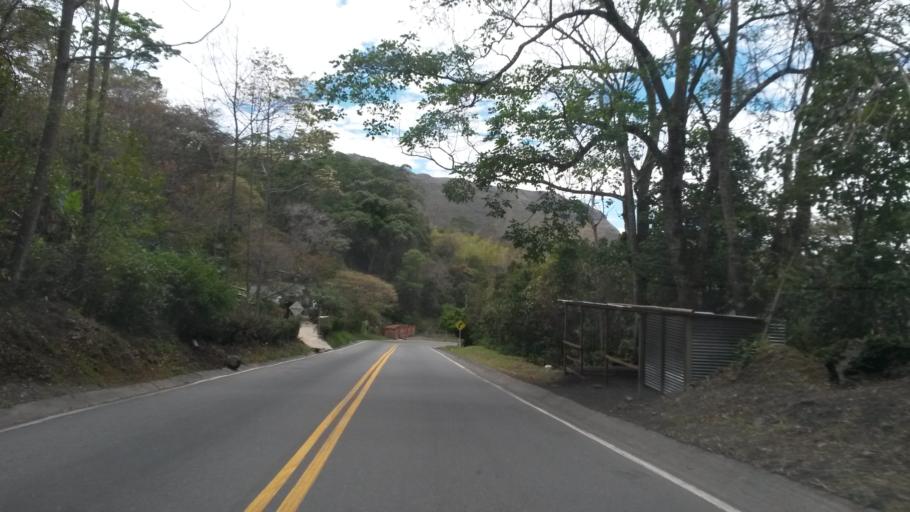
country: CO
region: Cauca
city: Rosas
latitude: 2.2769
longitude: -76.7207
